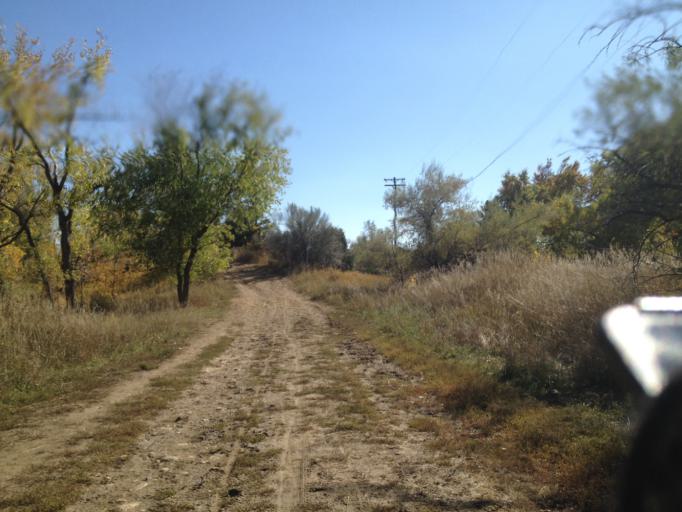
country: US
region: Colorado
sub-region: Boulder County
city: Boulder
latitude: 39.9824
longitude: -105.2356
